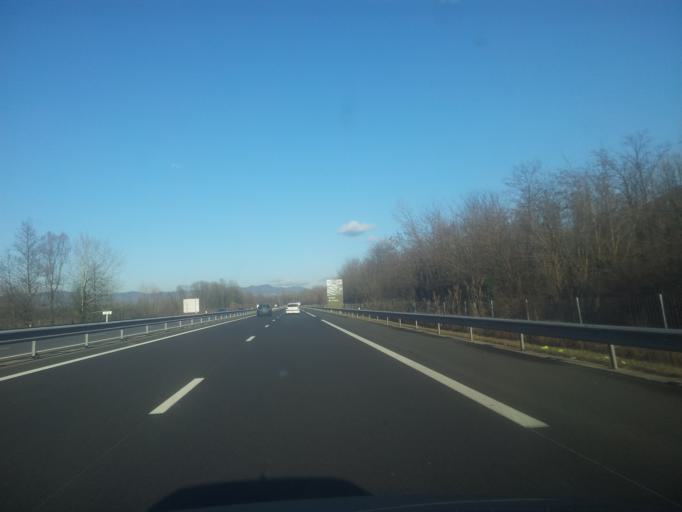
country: FR
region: Rhone-Alpes
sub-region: Departement de l'Isere
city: Saint-Quentin-sur-Isere
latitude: 45.2585
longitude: 5.5120
